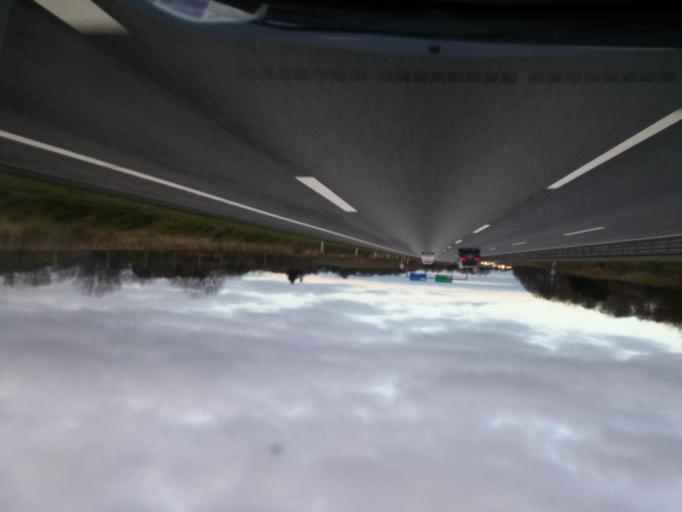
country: DK
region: South Denmark
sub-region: Vejle Kommune
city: Vejle
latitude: 55.6484
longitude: 9.5612
